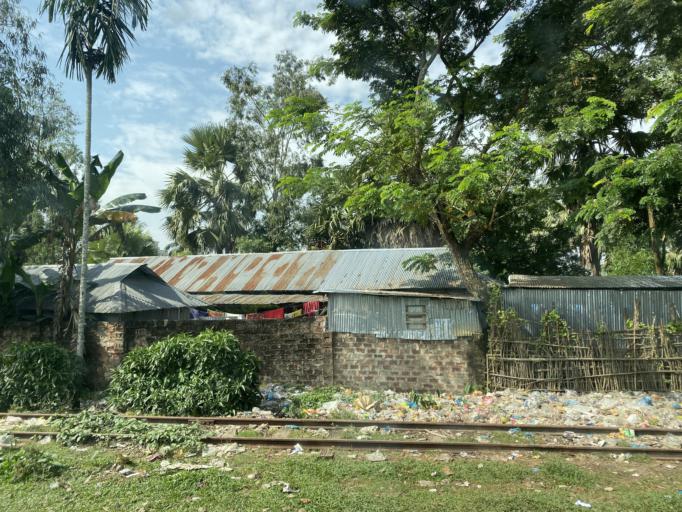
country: BD
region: Sylhet
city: Habiganj
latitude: 24.1798
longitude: 91.3568
